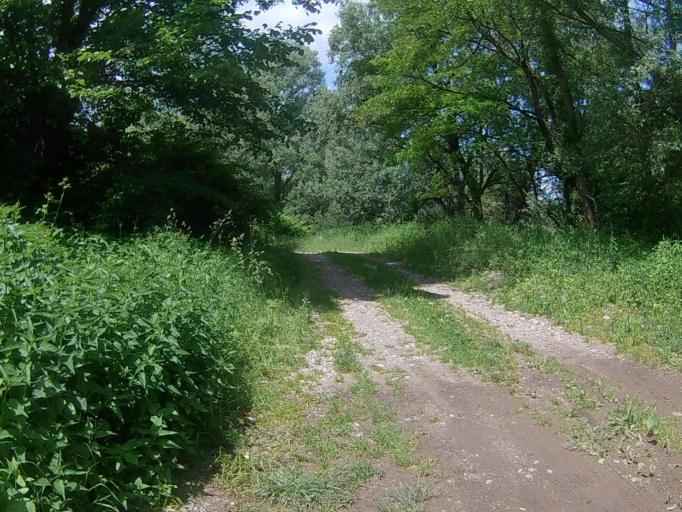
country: SI
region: Starse
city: Starse
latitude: 46.4725
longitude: 15.7704
